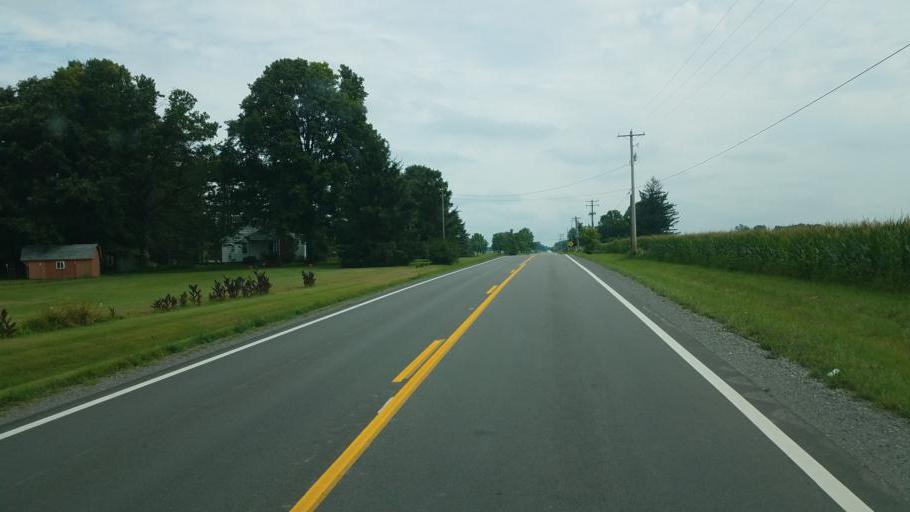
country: US
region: Ohio
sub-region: Marion County
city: Marion
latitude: 40.5247
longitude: -83.0573
